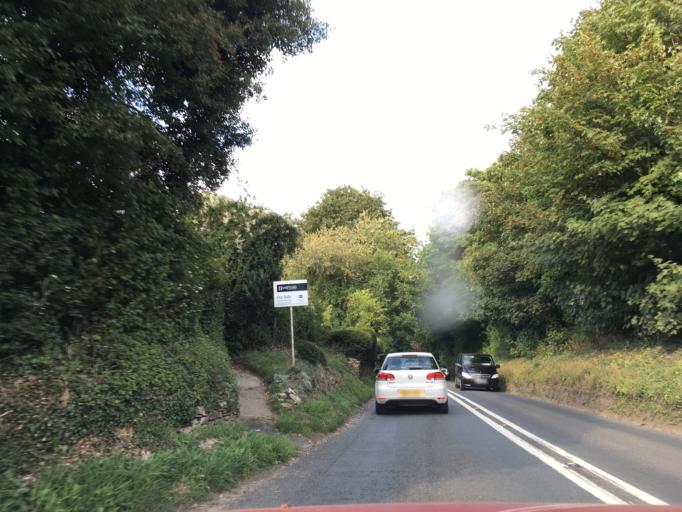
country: GB
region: England
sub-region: Gloucestershire
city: Coates
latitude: 51.6865
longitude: -2.0292
